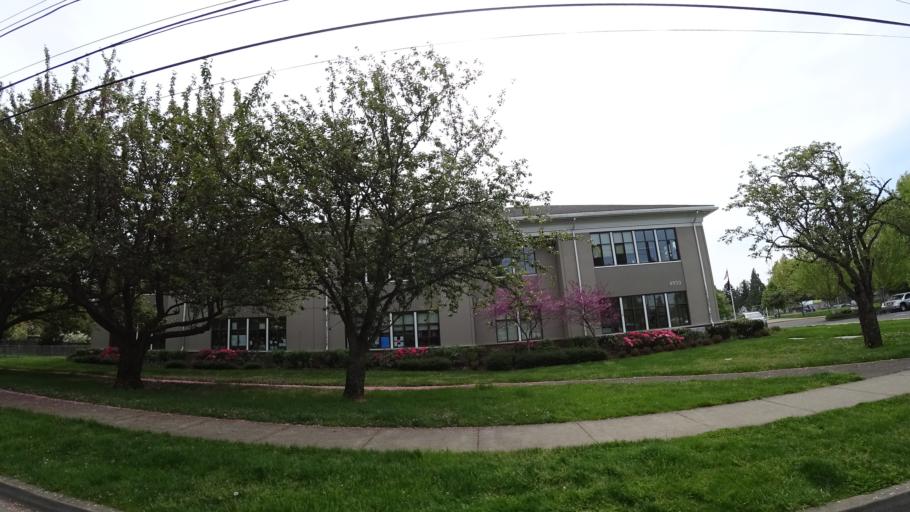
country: US
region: Oregon
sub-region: Clackamas County
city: Milwaukie
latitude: 45.4585
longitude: -122.6244
